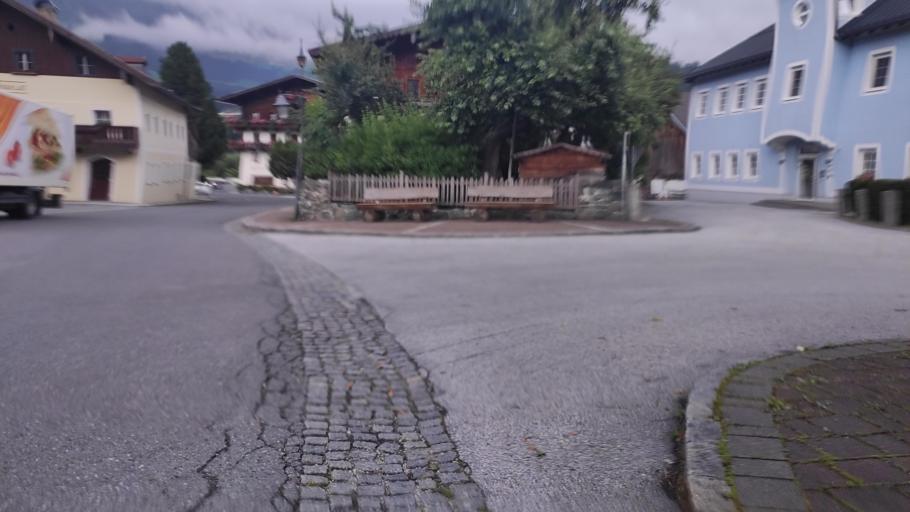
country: AT
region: Salzburg
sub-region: Politischer Bezirk Zell am See
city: Hollersbach im Pinzgau
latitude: 47.2753
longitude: 12.4196
